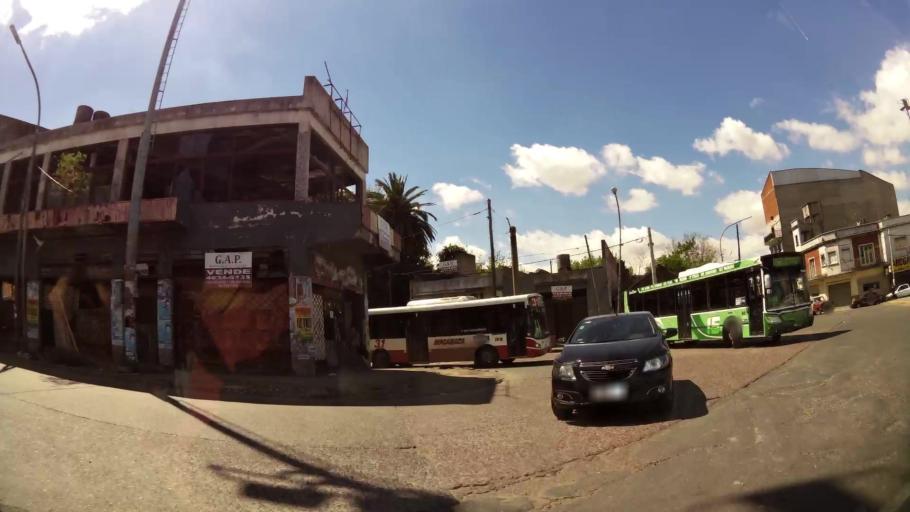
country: AR
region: Buenos Aires
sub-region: Partido de Lanus
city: Lanus
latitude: -34.6623
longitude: -58.4172
